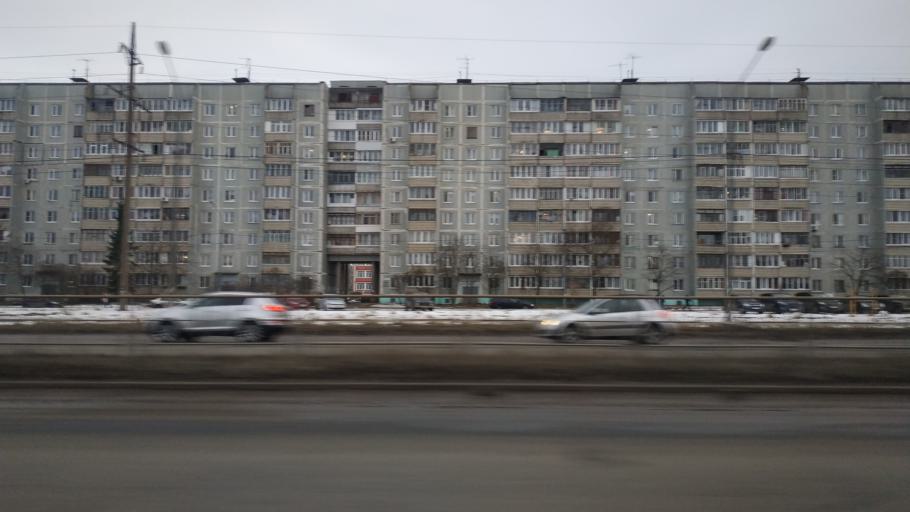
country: RU
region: Tverskaya
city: Tver
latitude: 56.8217
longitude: 35.8887
